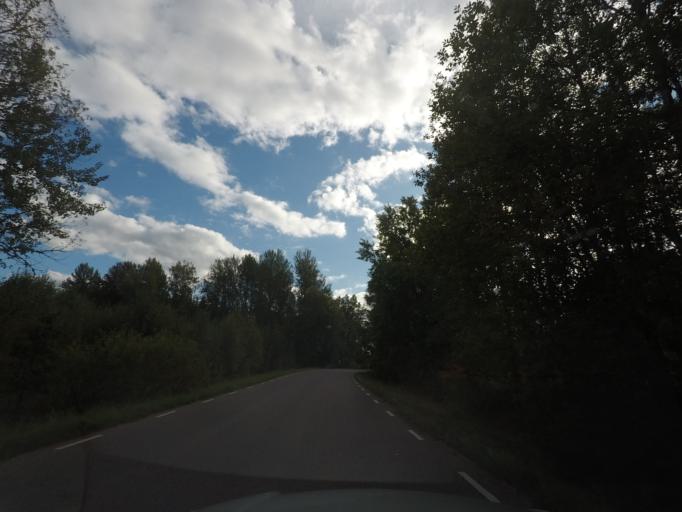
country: SE
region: Vaestmanland
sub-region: Hallstahammars Kommun
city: Kolback
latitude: 59.5216
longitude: 16.1906
